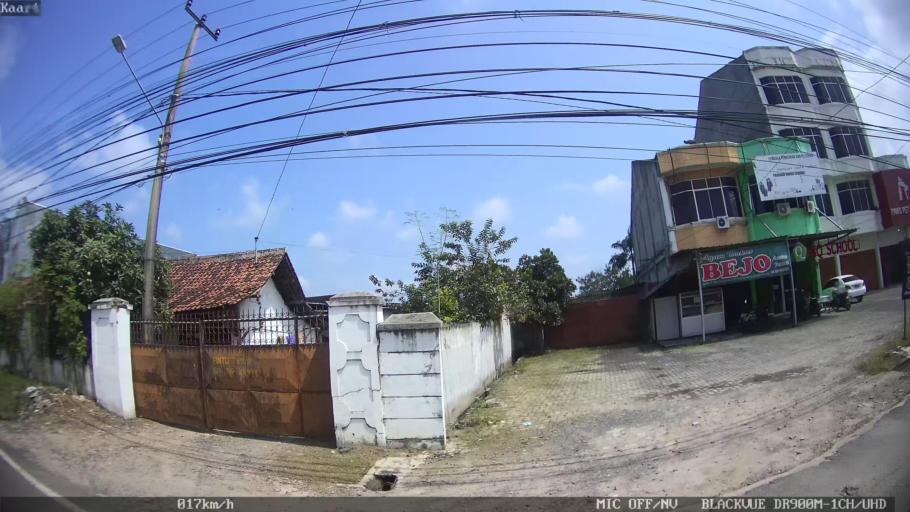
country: ID
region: Lampung
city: Kedaton
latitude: -5.3621
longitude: 105.2801
